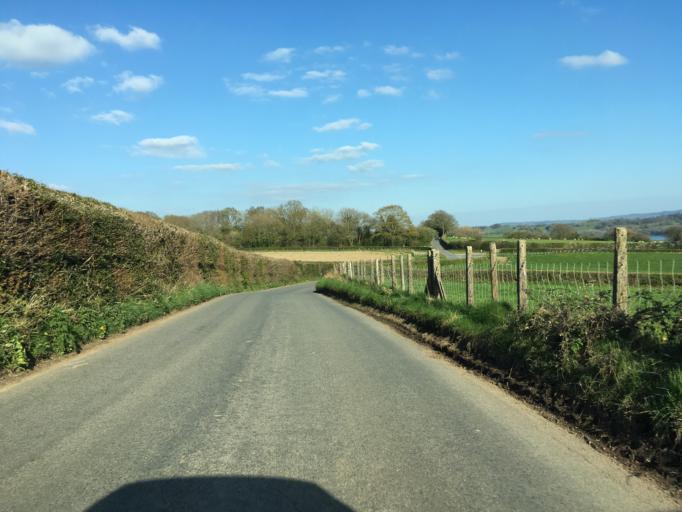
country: GB
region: Wales
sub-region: Torfaen County Borough
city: New Inn
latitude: 51.6992
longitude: -2.9934
